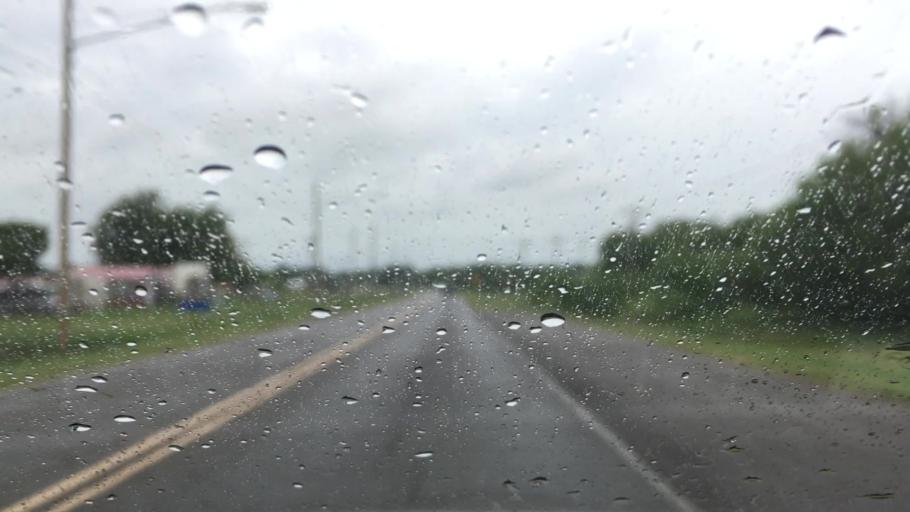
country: US
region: Oklahoma
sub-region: Cherokee County
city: Tahlequah
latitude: 35.9193
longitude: -94.9976
